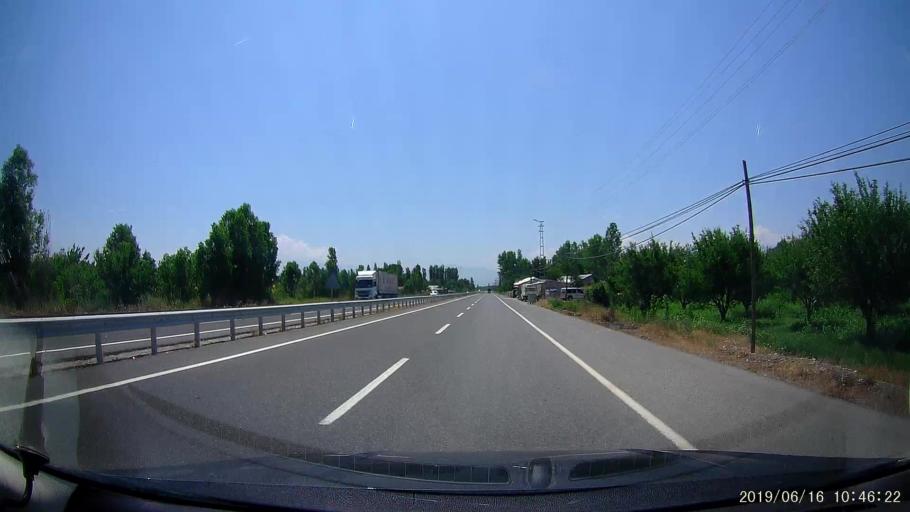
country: AM
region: Armavir
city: Shenavan
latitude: 40.0225
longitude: 43.8788
